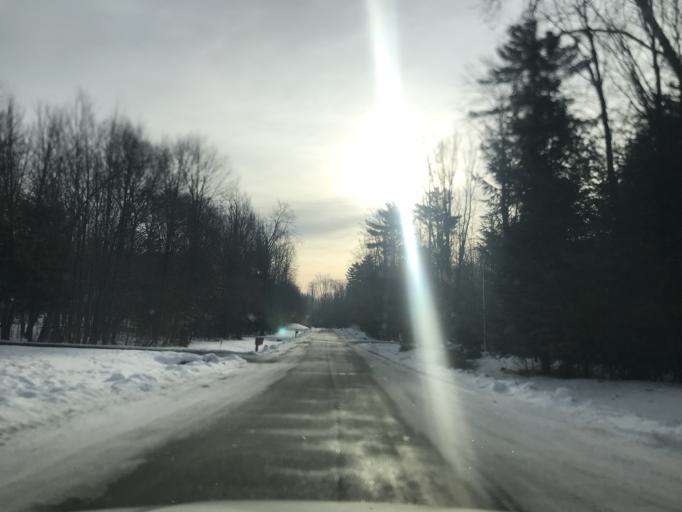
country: US
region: Wisconsin
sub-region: Brown County
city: Suamico
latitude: 44.6878
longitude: -88.0630
